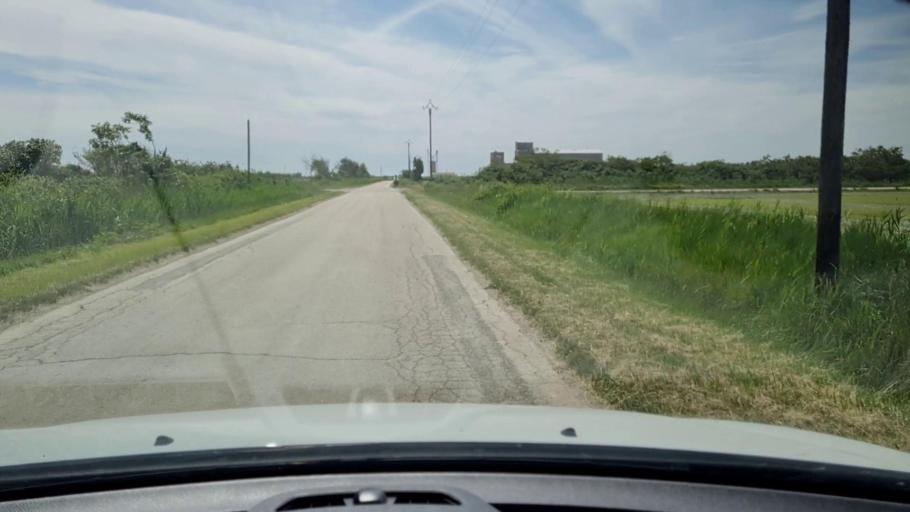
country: FR
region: Languedoc-Roussillon
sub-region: Departement du Gard
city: Saint-Gilles
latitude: 43.5863
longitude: 4.4179
